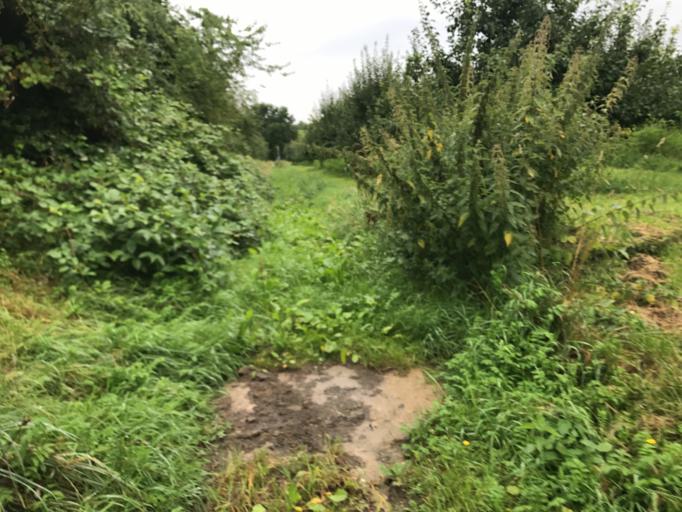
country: DE
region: Rheinland-Pfalz
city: Wackernheim
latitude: 49.9953
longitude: 8.1328
